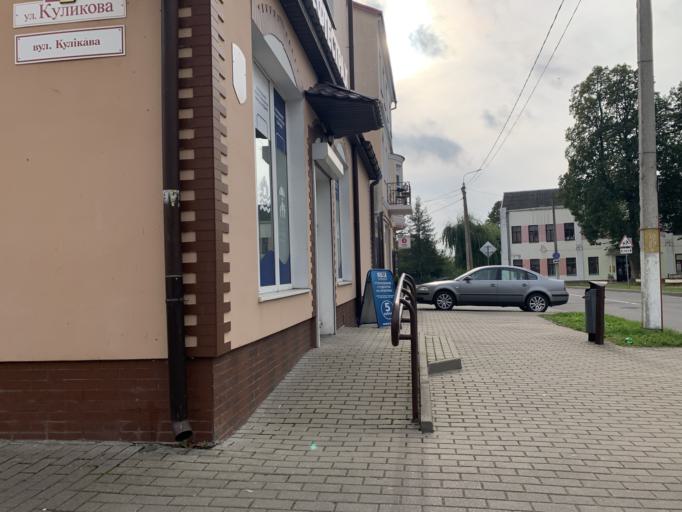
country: BY
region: Brest
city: Pinsk
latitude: 52.1156
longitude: 26.1143
